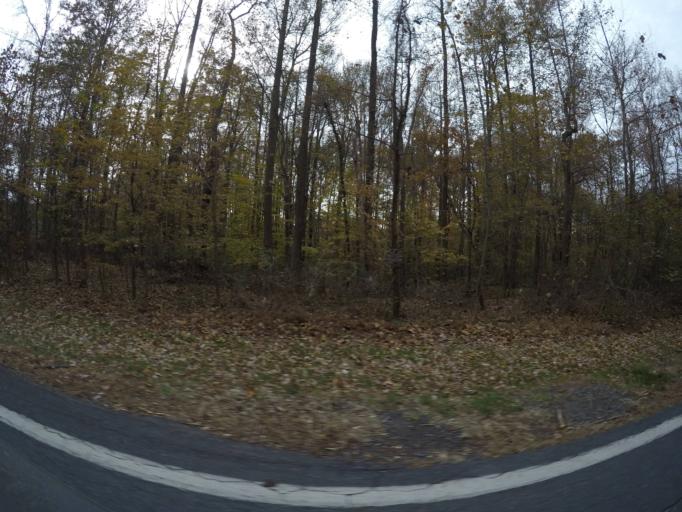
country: US
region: Maryland
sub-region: Harford County
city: Riverside
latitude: 39.4586
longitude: -76.2702
